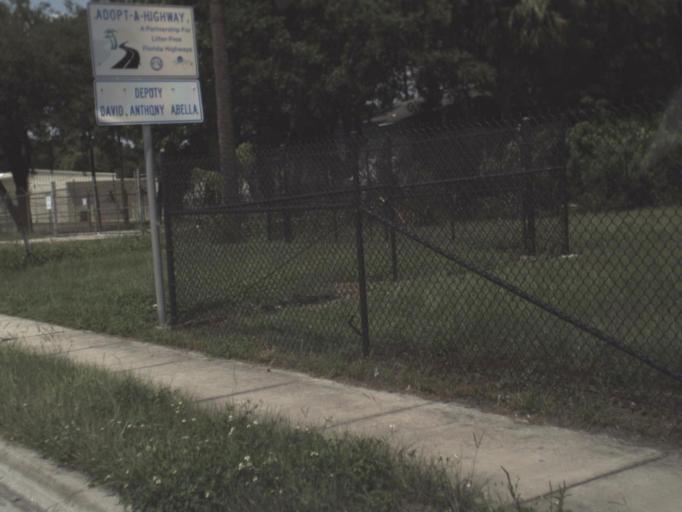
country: US
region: Florida
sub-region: Hillsborough County
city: Palm River-Clair Mel
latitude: 27.9237
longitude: -82.4018
